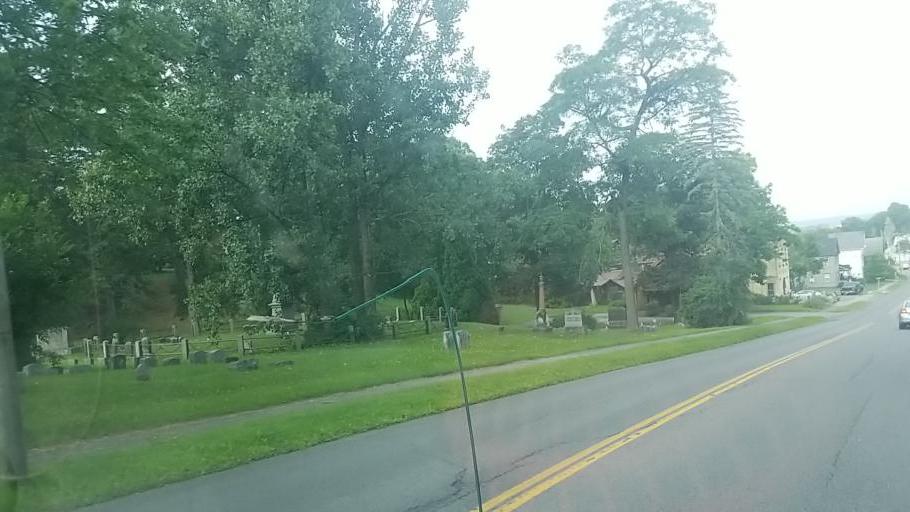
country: US
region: New York
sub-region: Fulton County
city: Gloversville
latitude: 43.0507
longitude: -74.3349
